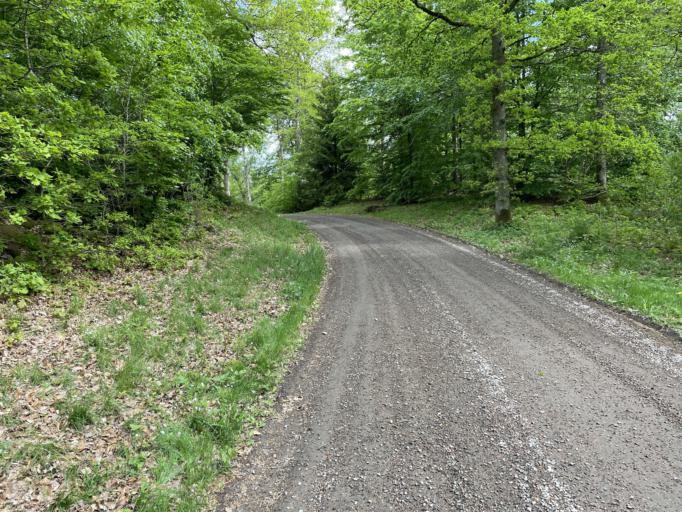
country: SE
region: Skane
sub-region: Klippans Kommun
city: Klippan
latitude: 56.1608
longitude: 13.1432
